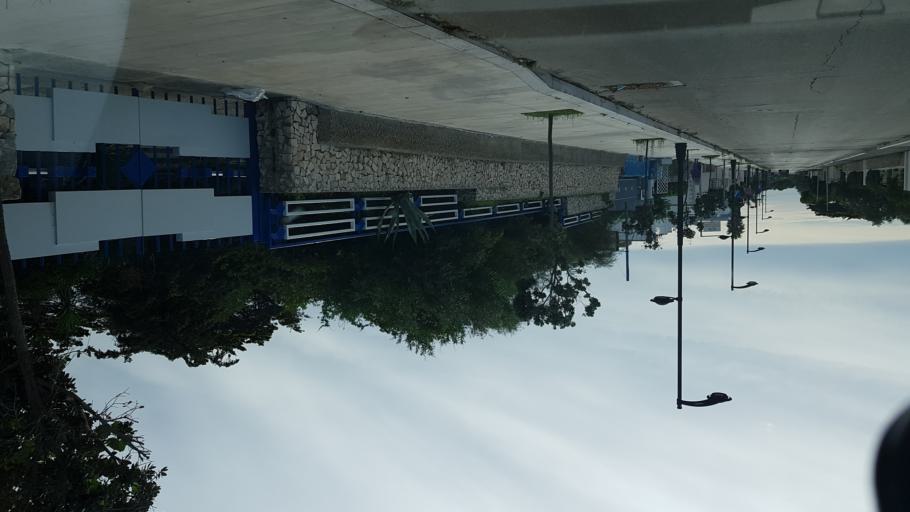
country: IT
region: Apulia
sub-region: Provincia di Lecce
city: Borgagne
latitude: 40.3003
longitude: 18.4065
